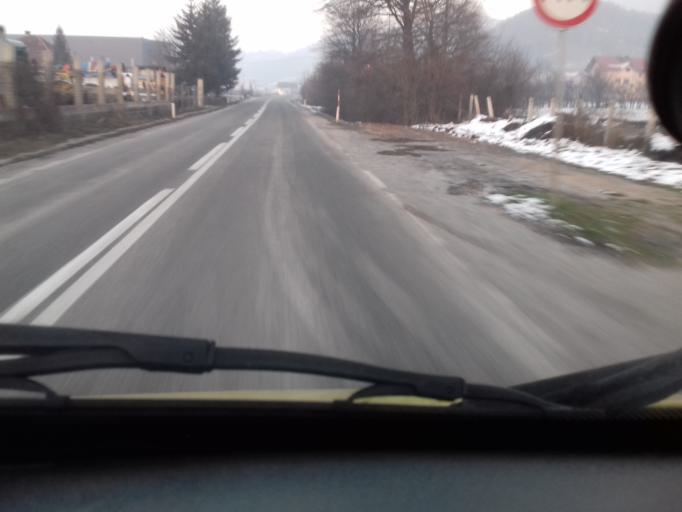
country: BA
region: Federation of Bosnia and Herzegovina
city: Vogosca
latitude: 43.8822
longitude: 18.3188
